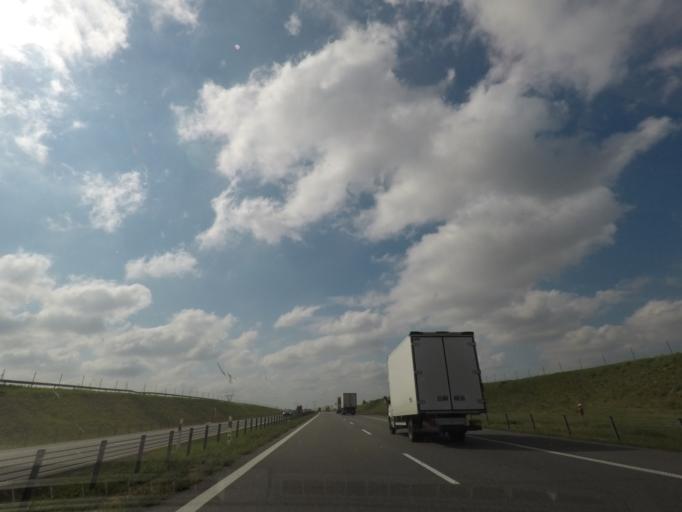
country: PL
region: Kujawsko-Pomorskie
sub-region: Powiat chelminski
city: Lisewo
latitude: 53.2413
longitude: 18.7249
